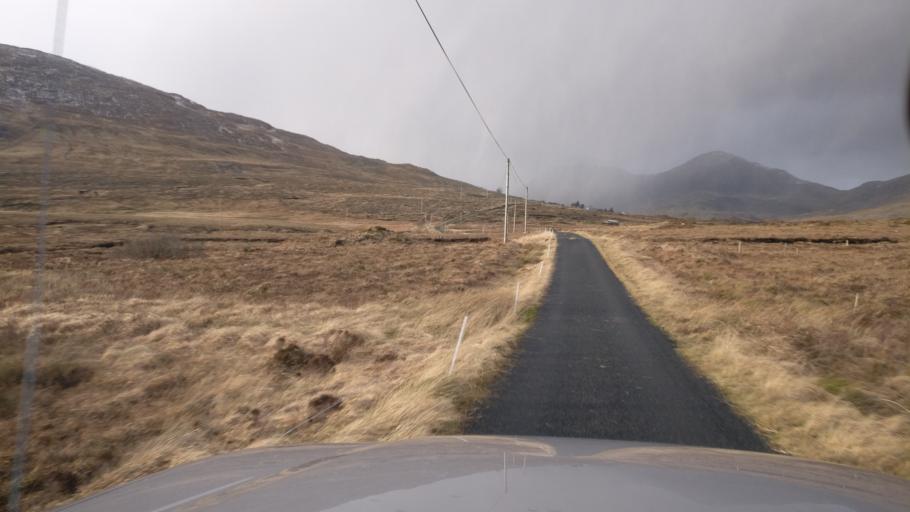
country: IE
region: Connaught
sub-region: County Galway
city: Clifden
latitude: 53.4771
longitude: -9.6931
